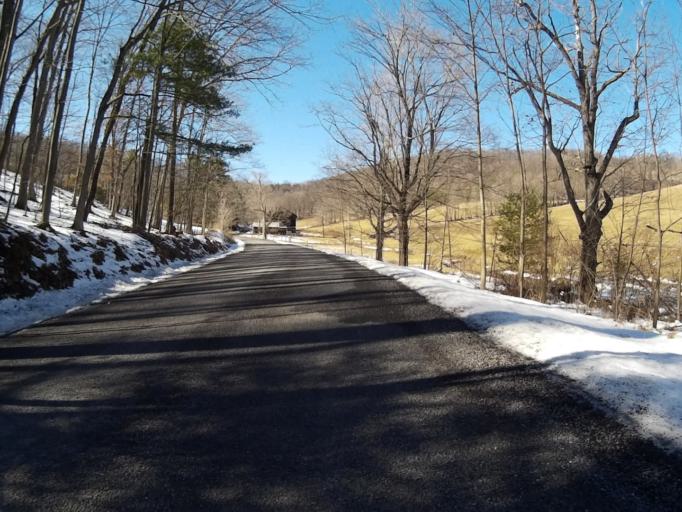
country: US
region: Pennsylvania
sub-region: Centre County
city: Stormstown
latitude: 40.8474
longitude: -78.0332
